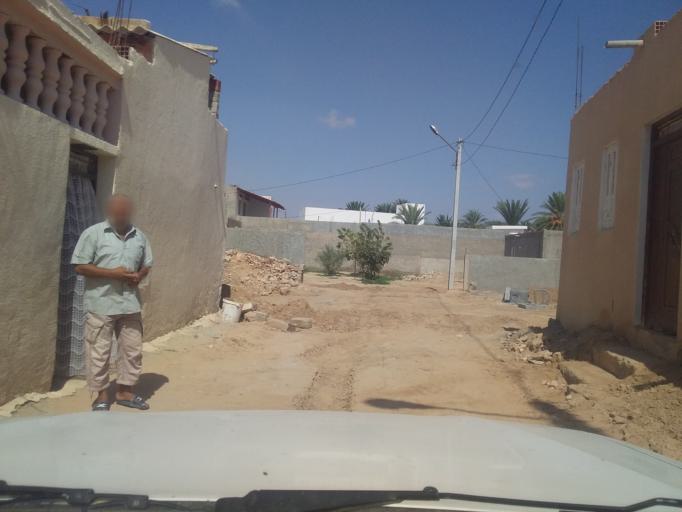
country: TN
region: Qabis
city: Gabes
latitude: 33.6229
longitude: 10.2870
